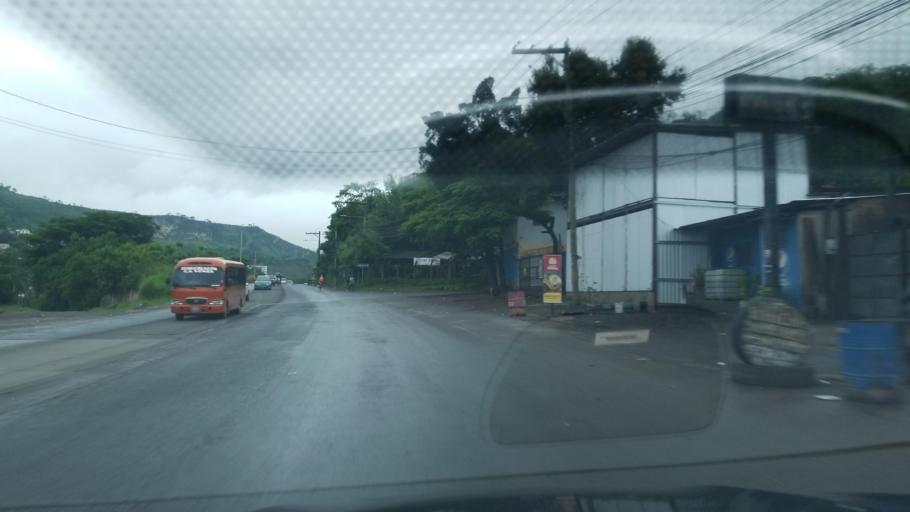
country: HN
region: Francisco Morazan
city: Yaguacire
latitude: 14.0417
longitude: -87.2110
